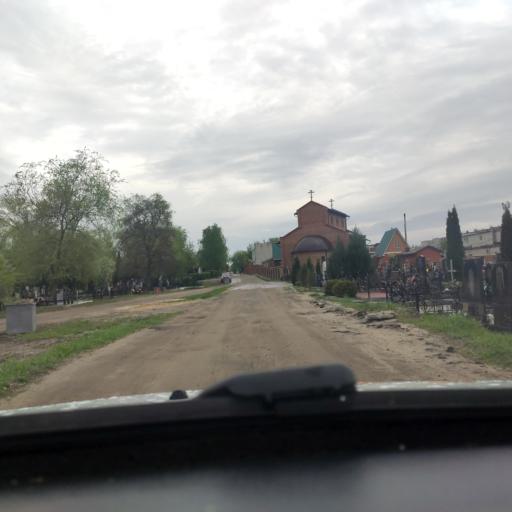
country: RU
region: Voronezj
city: Somovo
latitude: 51.6636
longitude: 39.2920
